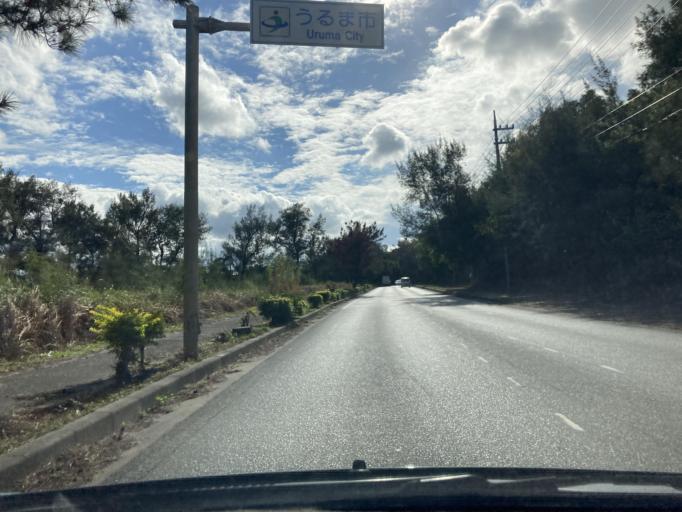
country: JP
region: Okinawa
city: Ishikawa
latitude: 26.4337
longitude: 127.8076
